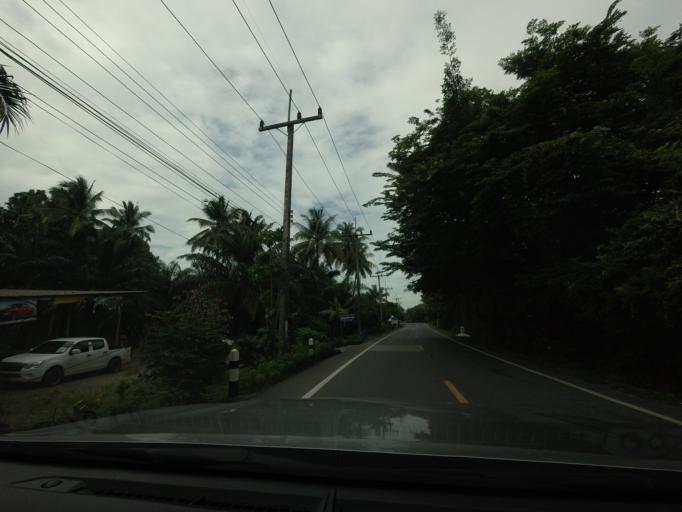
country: TH
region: Nakhon Si Thammarat
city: Phra Phrom
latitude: 8.2892
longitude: 99.9458
